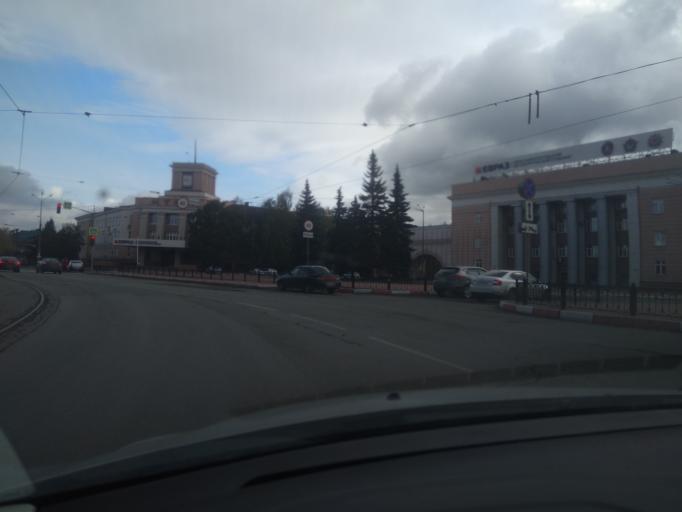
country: RU
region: Sverdlovsk
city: Nizhniy Tagil
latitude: 57.9284
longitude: 60.0102
